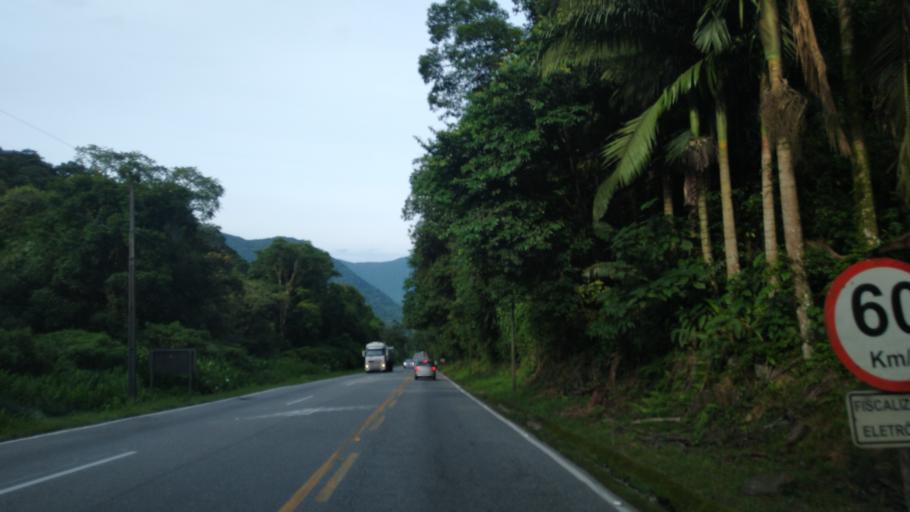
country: BR
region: Santa Catarina
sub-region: Joinville
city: Joinville
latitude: -26.1860
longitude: -49.0236
